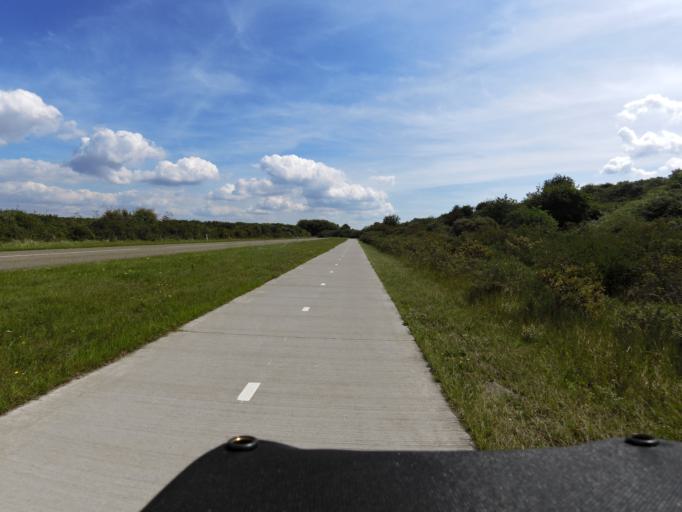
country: NL
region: Zeeland
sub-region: Schouwen-Duiveland
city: Scharendijke
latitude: 51.7843
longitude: 3.8766
